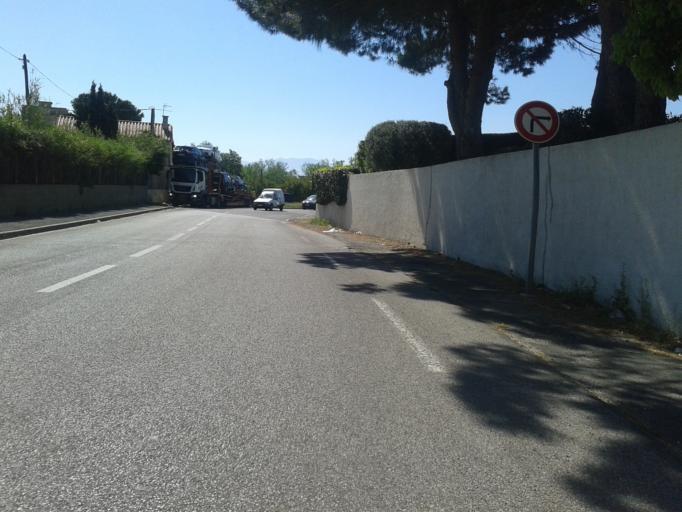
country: FR
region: Languedoc-Roussillon
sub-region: Departement des Pyrenees-Orientales
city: Perpignan
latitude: 42.6788
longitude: 2.8942
